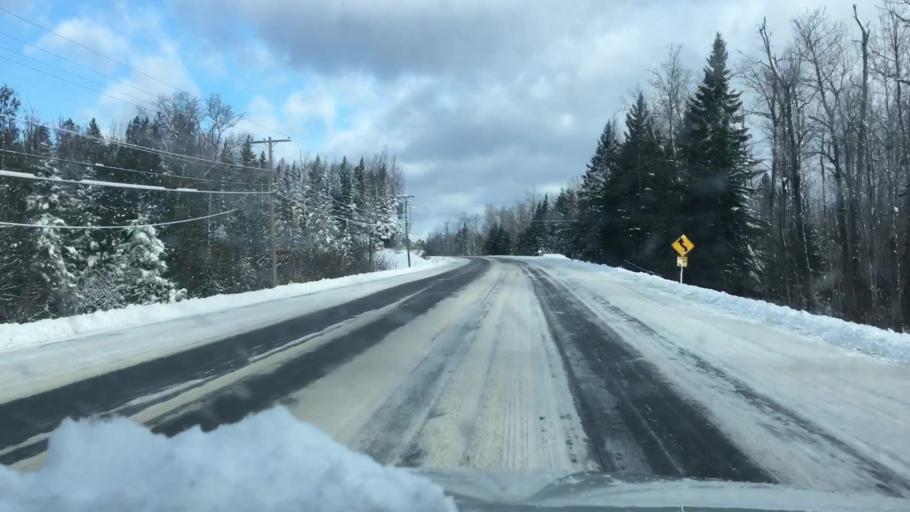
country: US
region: Maine
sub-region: Aroostook County
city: Caribou
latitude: 46.9238
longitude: -68.0200
